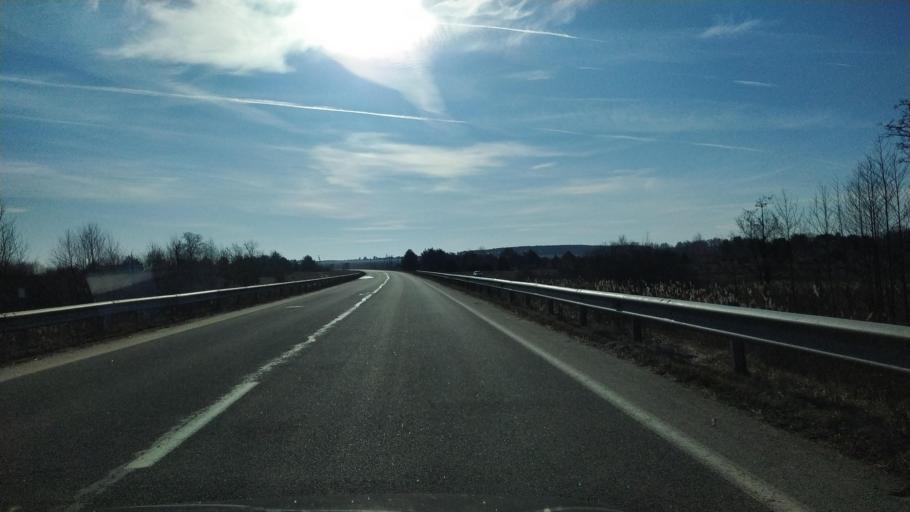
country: BY
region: Brest
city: Kamyanyets
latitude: 52.4263
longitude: 23.8379
